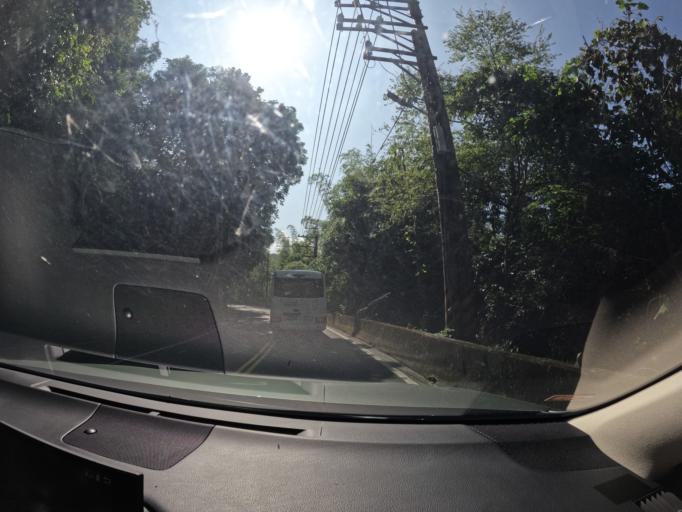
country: TW
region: Taiwan
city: Yujing
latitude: 23.0705
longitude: 120.6508
